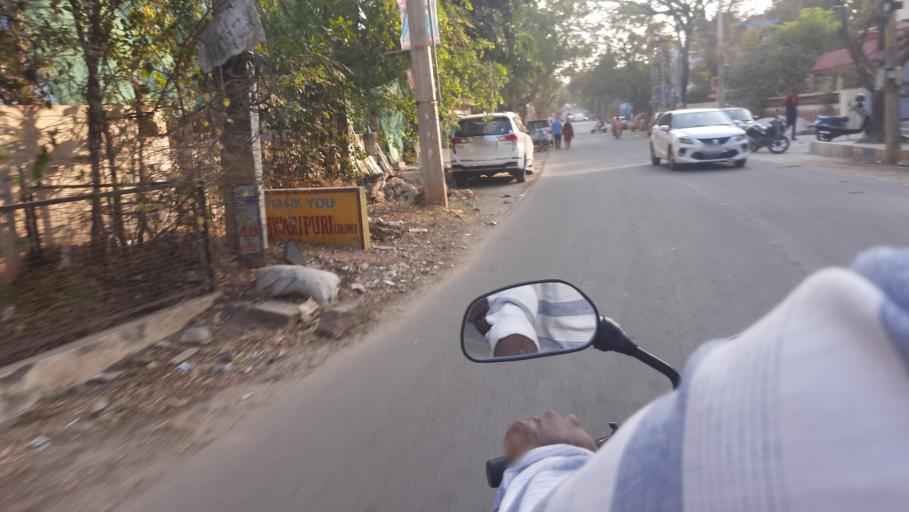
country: IN
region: Telangana
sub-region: Rangareddi
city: Secunderabad
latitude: 17.4896
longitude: 78.5497
